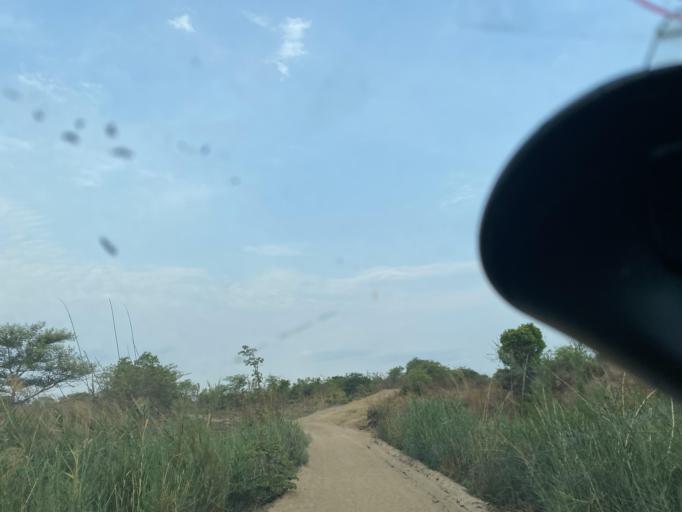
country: ZM
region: Lusaka
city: Chongwe
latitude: -15.2080
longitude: 28.5049
